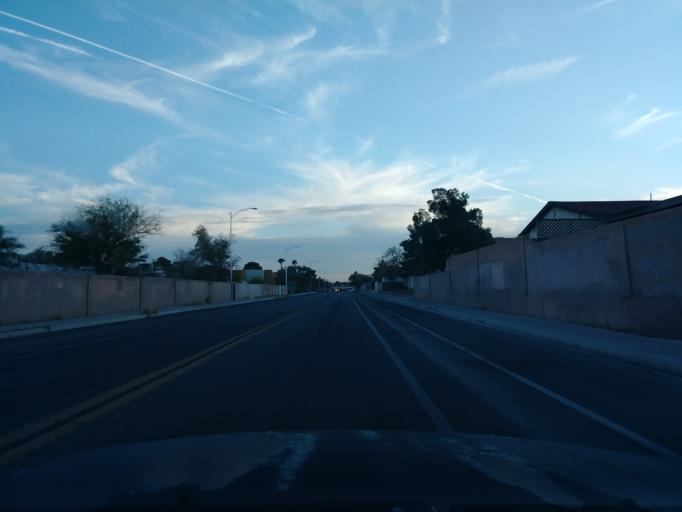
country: US
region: Nevada
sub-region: Clark County
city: Spring Valley
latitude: 36.1634
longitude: -115.2421
